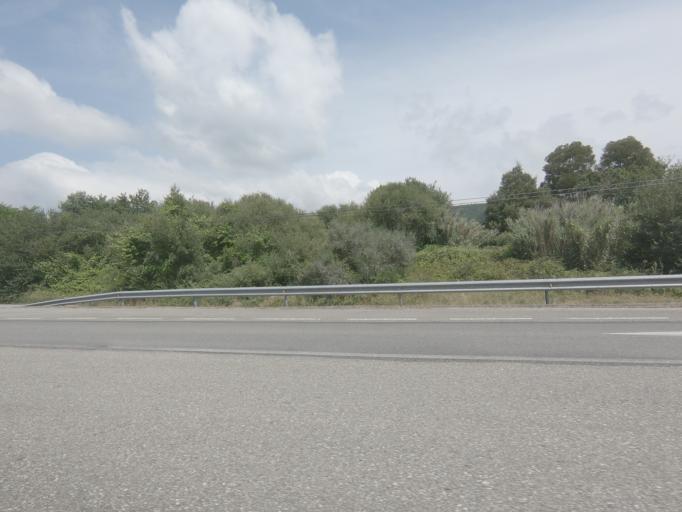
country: ES
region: Galicia
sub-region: Provincia de Pontevedra
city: Tomino
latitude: 42.0259
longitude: -8.7329
